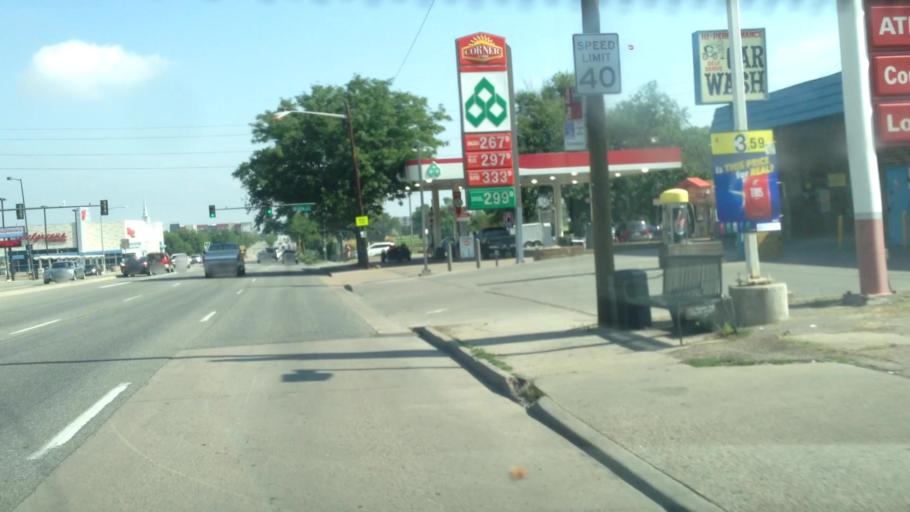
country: US
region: Colorado
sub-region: Adams County
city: Commerce City
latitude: 39.7647
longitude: -104.9404
